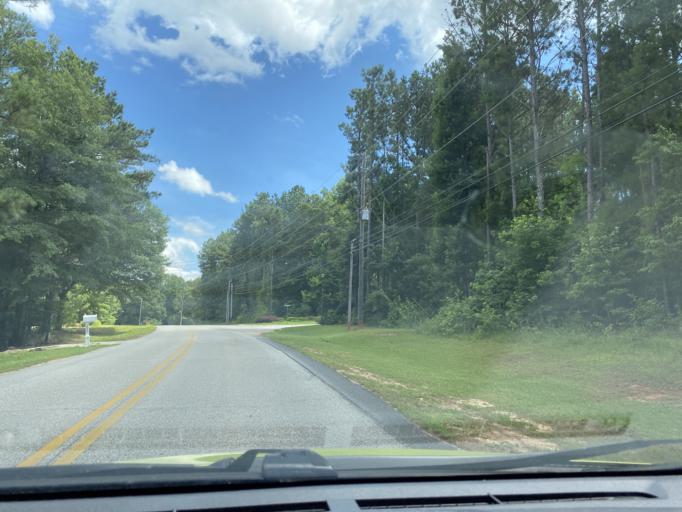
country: US
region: Georgia
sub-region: Fayette County
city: Peachtree City
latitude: 33.4148
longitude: -84.6945
